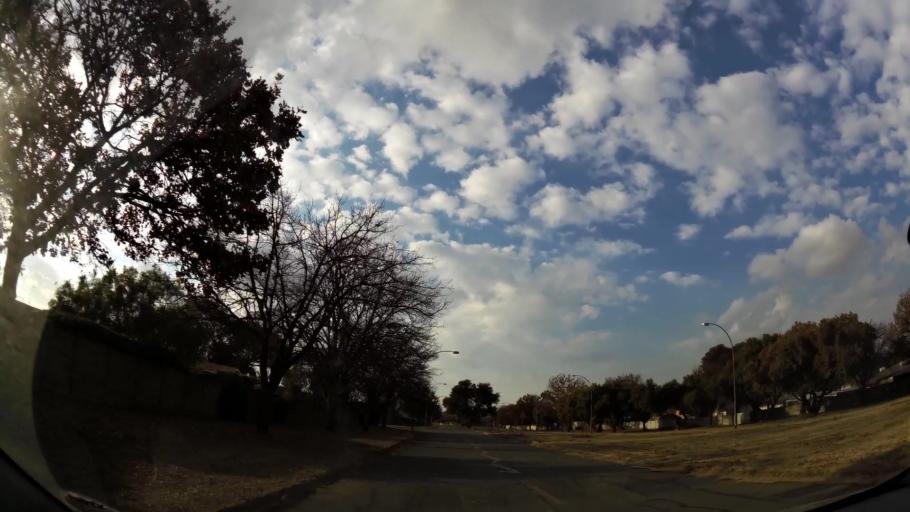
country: ZA
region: Orange Free State
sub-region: Fezile Dabi District Municipality
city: Sasolburg
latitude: -26.8193
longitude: 27.8087
